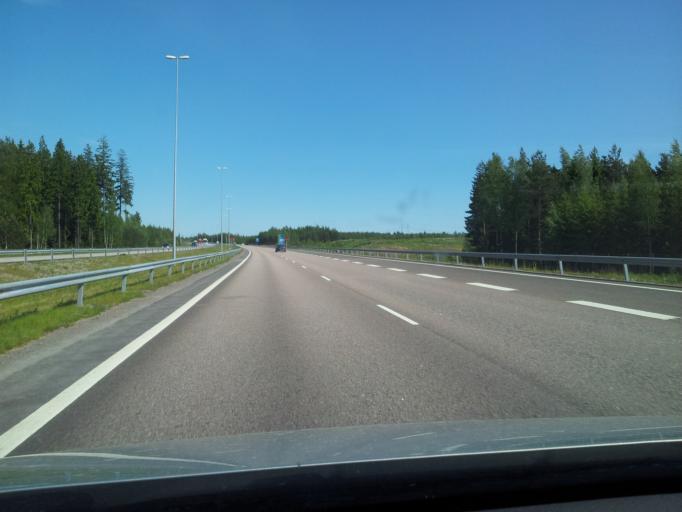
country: FI
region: Uusimaa
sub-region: Loviisa
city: Lovisa
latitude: 60.4610
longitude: 26.1529
